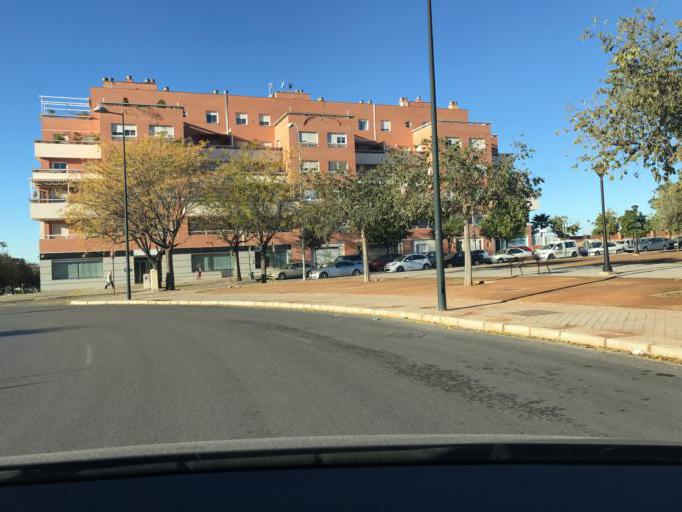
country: ES
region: Andalusia
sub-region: Provincia de Granada
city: Maracena
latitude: 37.2032
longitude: -3.6208
